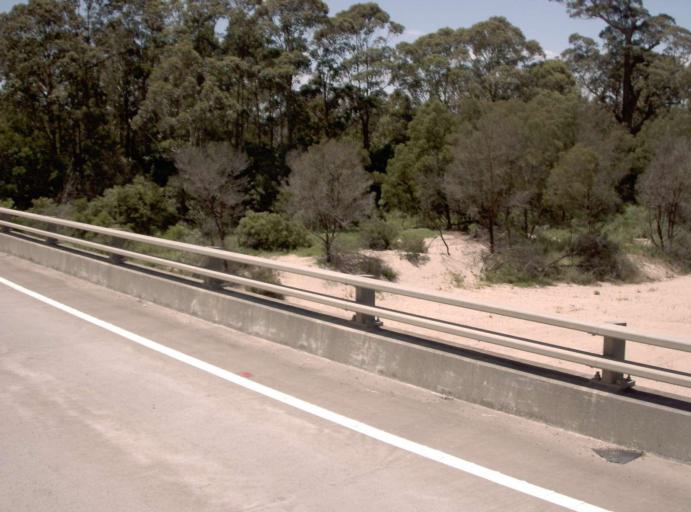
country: AU
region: Victoria
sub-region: East Gippsland
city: Lakes Entrance
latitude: -37.7157
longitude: 148.4538
